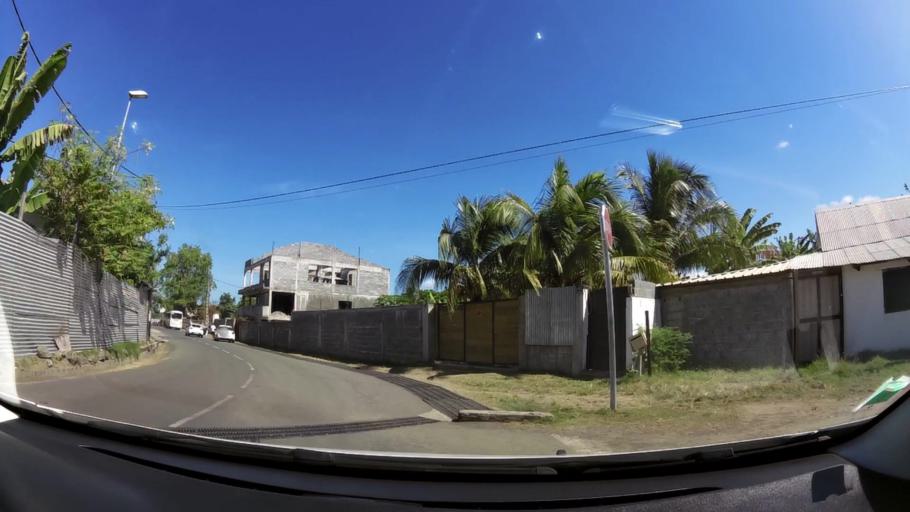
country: YT
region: Pamandzi
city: Pamandzi
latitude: -12.7967
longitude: 45.2788
